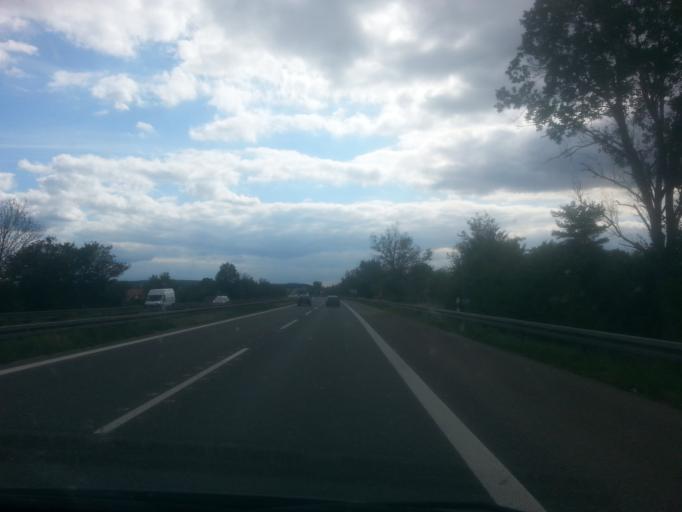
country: DE
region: Bavaria
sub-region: Upper Palatinate
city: Stulln
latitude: 49.4155
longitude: 12.1657
